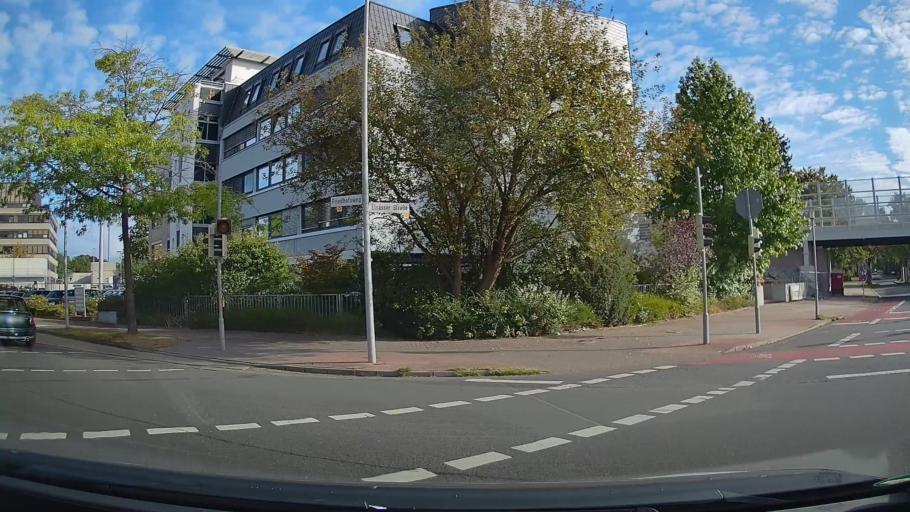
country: DE
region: Lower Saxony
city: Oldenburg
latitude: 53.1514
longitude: 8.2006
